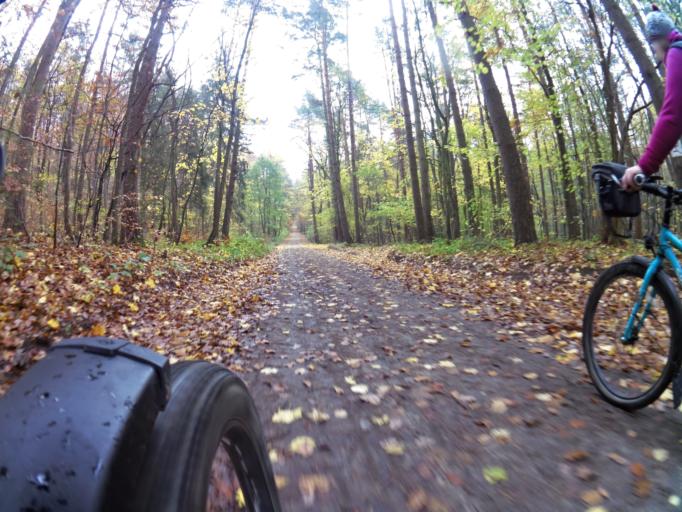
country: PL
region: Pomeranian Voivodeship
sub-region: Powiat pucki
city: Krokowa
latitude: 54.7819
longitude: 18.0886
